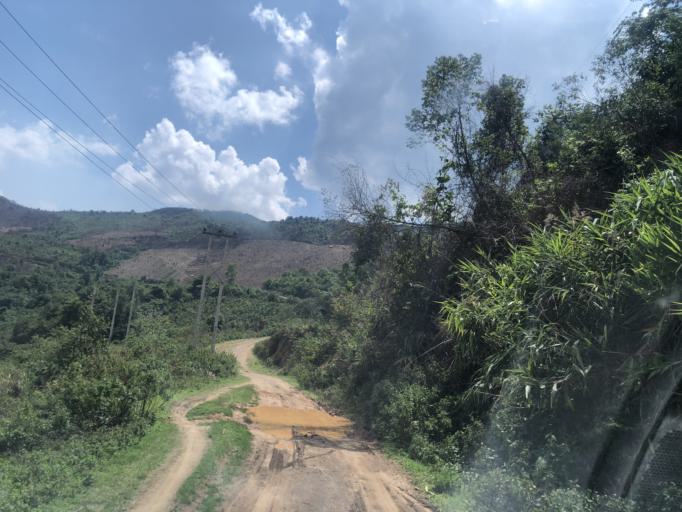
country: LA
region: Phongsali
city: Phongsali
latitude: 21.3964
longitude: 102.2236
